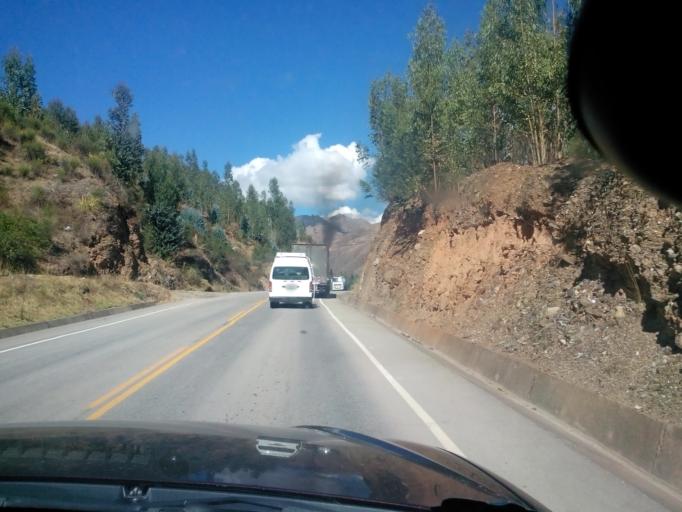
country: PE
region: Cusco
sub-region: Provincia de Quispicanchis
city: Urcos
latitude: -13.6896
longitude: -71.5948
